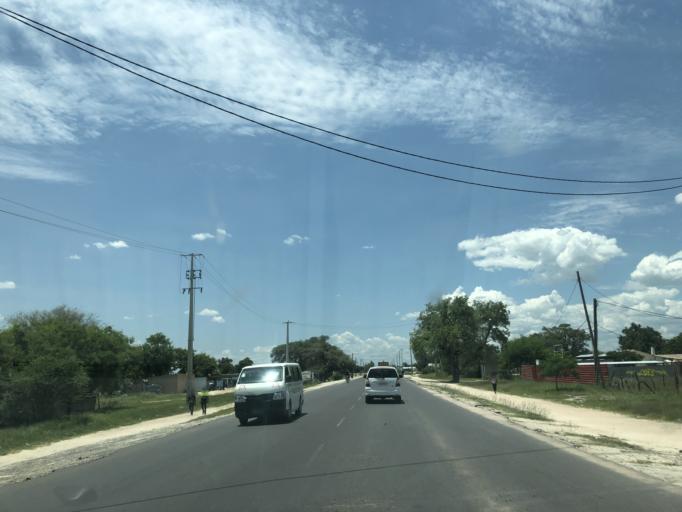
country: AO
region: Cunene
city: Ondjiva
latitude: -17.0626
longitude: 15.7383
